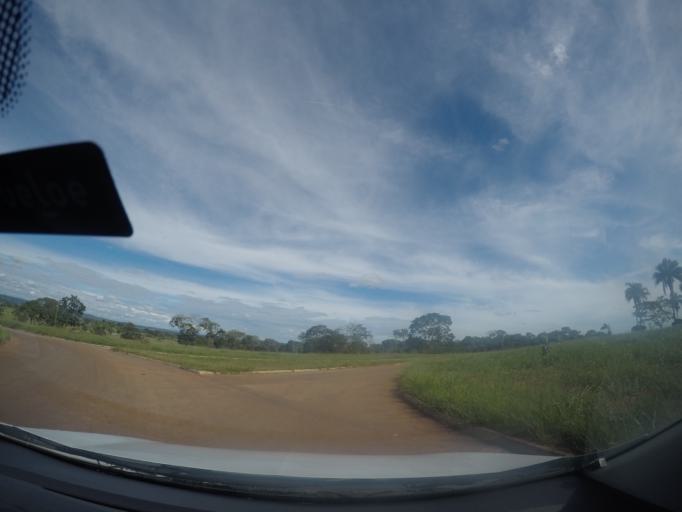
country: BR
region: Goias
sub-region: Inhumas
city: Inhumas
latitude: -16.4035
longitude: -49.4697
